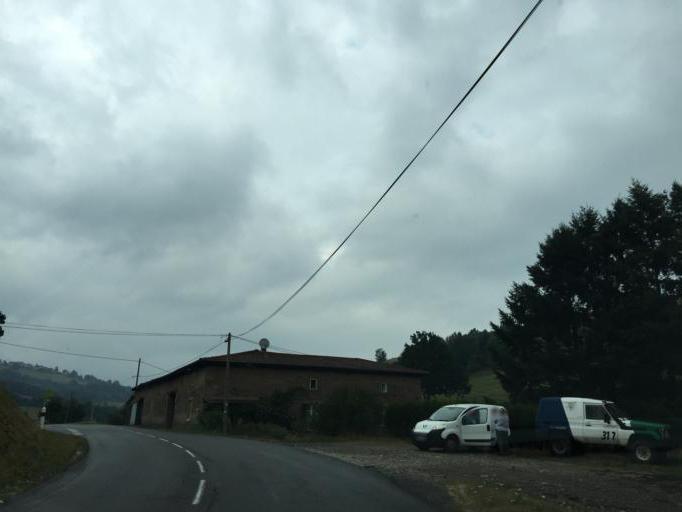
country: FR
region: Rhone-Alpes
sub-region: Departement de la Loire
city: Saint-Christo-en-Jarez
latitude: 45.5302
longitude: 4.4754
